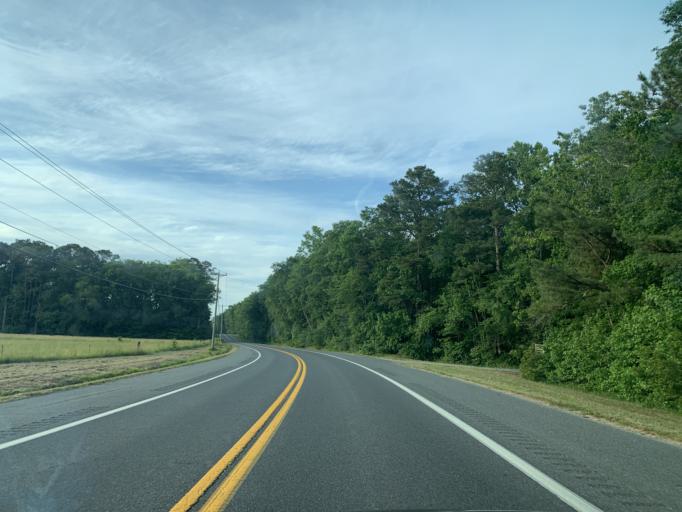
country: US
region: Maryland
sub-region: Worcester County
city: Snow Hill
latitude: 38.0823
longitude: -75.3988
